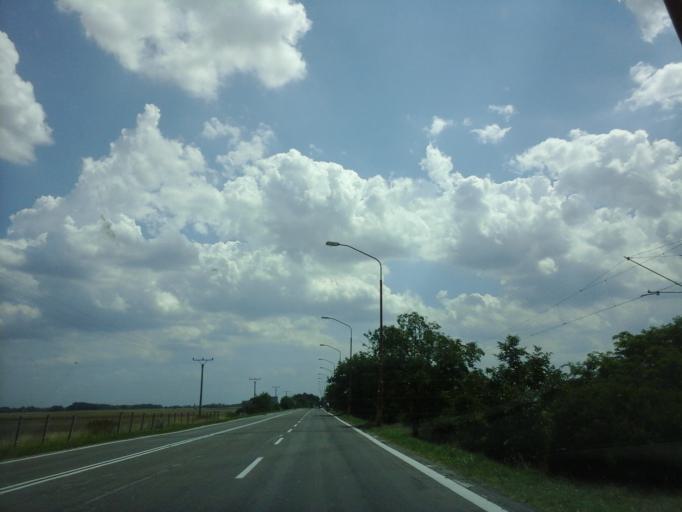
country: HU
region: Gyor-Moson-Sopron
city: Rajka
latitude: 48.0250
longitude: 17.1711
